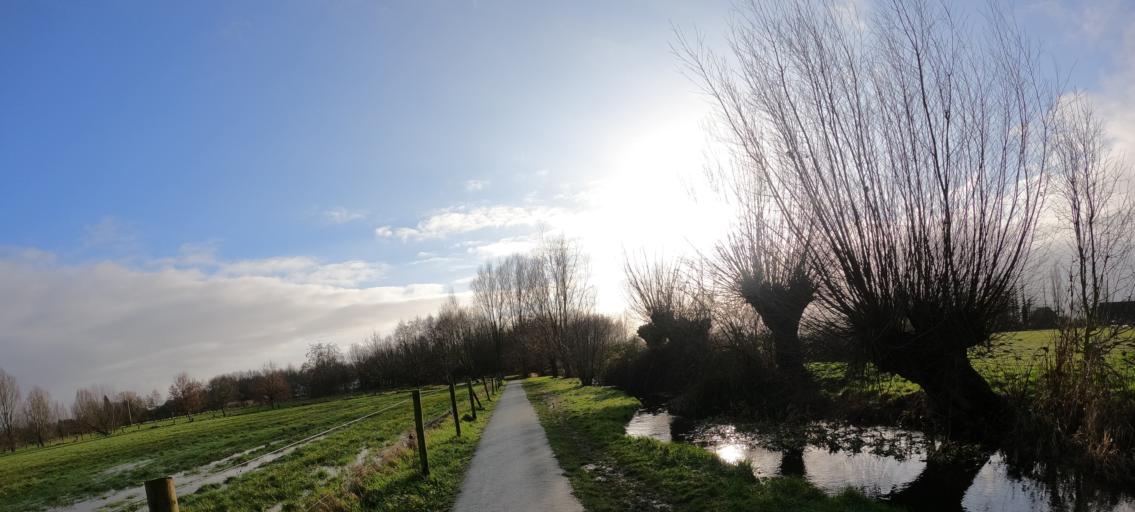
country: BE
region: Flanders
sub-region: Provincie Antwerpen
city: Borsbeek
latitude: 51.1911
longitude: 4.4806
